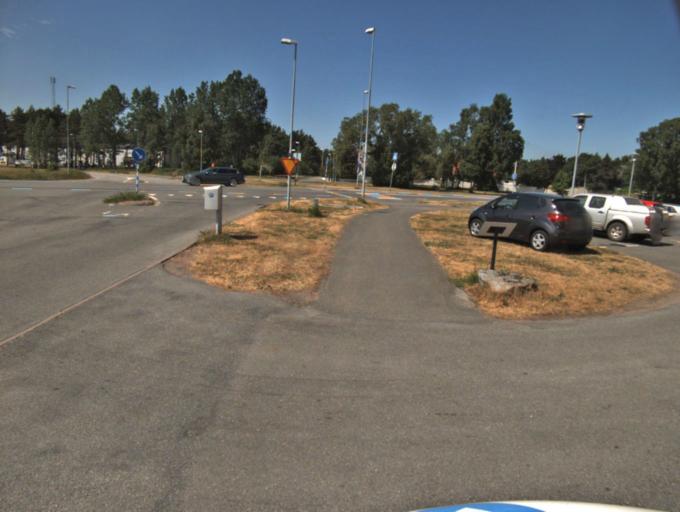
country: SE
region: Skane
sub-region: Kristianstads Kommun
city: Ahus
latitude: 55.9170
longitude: 14.2774
